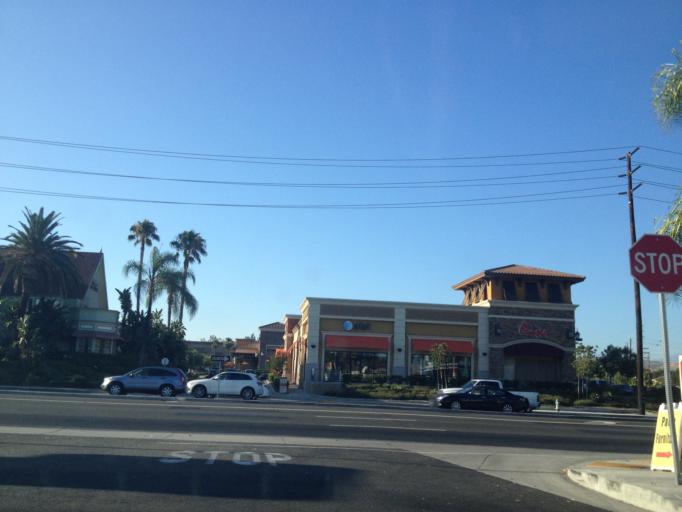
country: US
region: California
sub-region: Orange County
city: Brea
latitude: 33.9105
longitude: -117.8809
